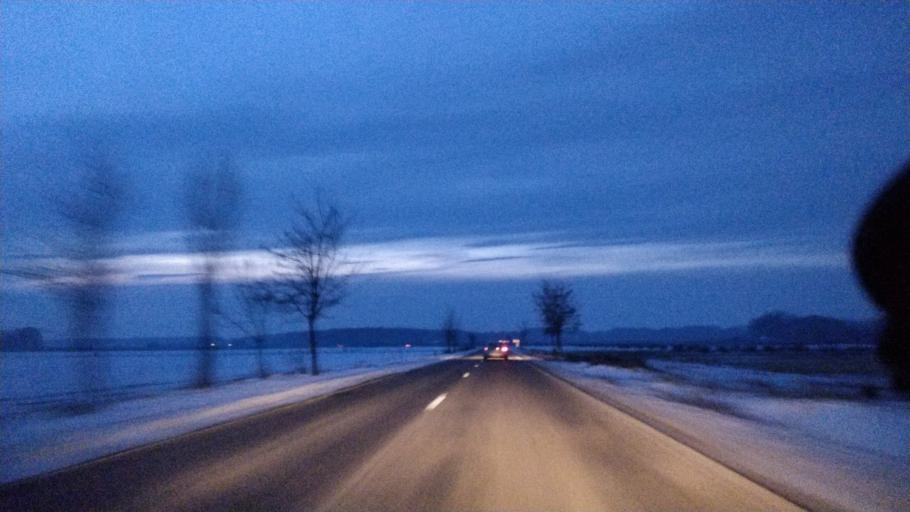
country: RO
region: Vrancea
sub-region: Comuna Suraia
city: Suraia
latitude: 45.6477
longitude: 27.3495
